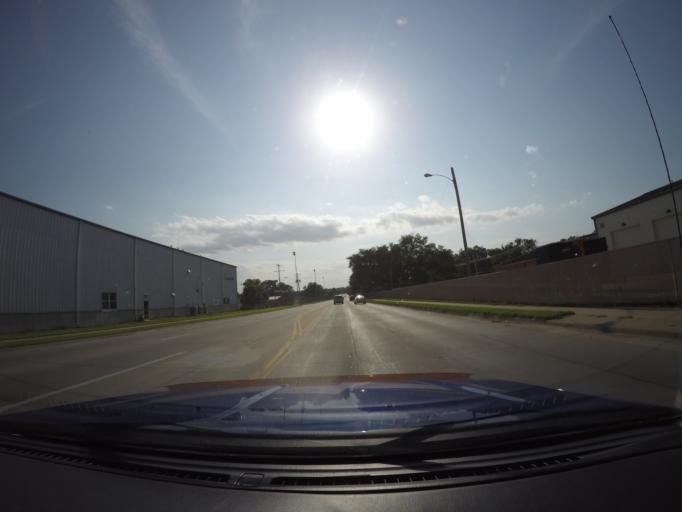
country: US
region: Kansas
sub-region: Riley County
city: Manhattan
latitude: 39.1743
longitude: -96.5725
